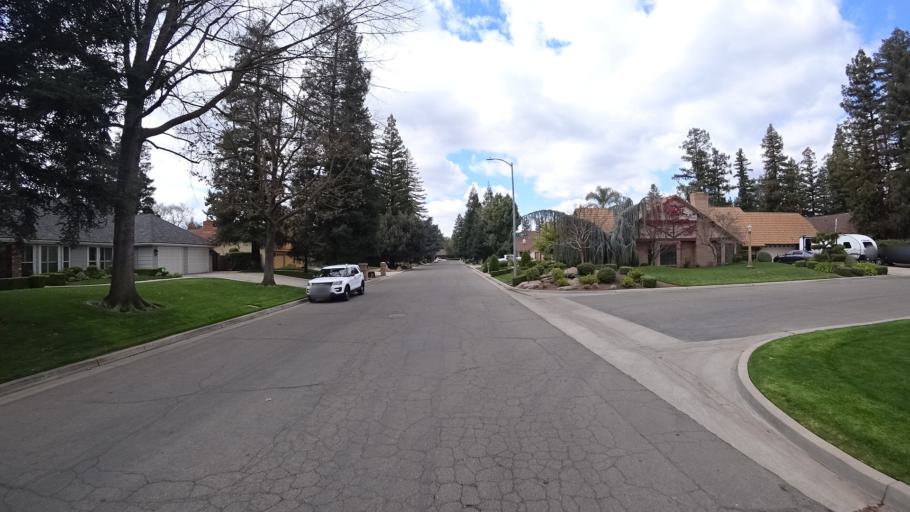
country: US
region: California
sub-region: Fresno County
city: Fresno
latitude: 36.8276
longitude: -119.8414
